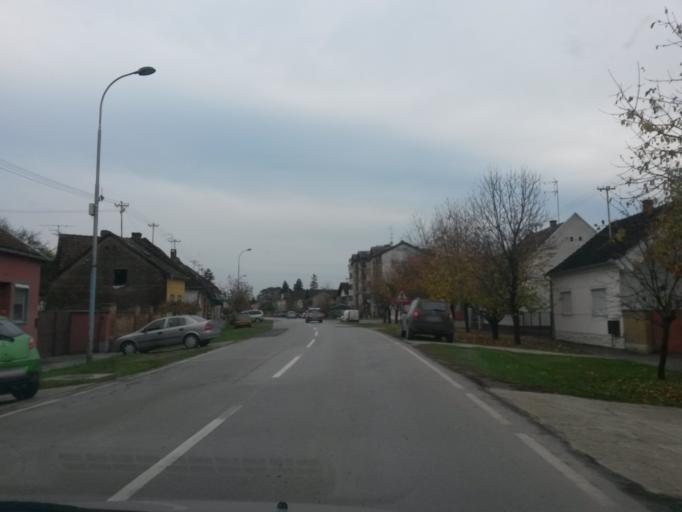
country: HR
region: Osjecko-Baranjska
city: Darda
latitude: 45.6280
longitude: 18.6867
